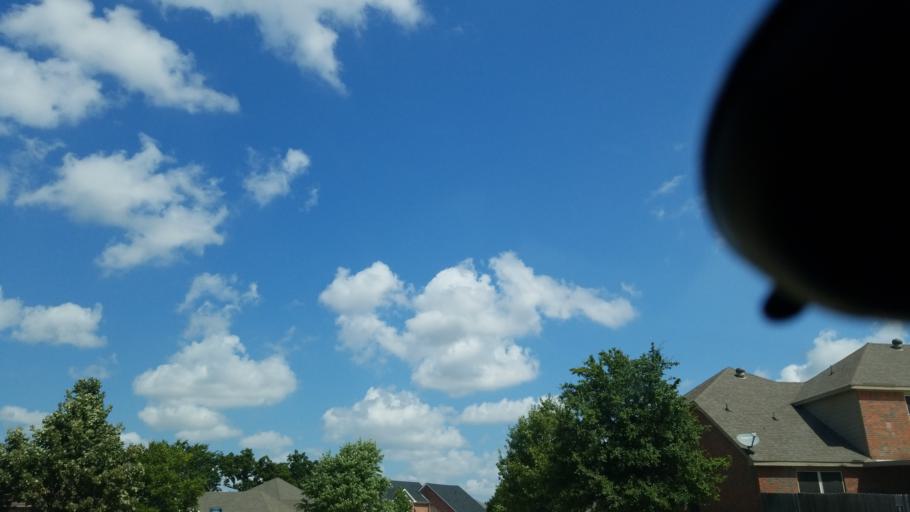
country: US
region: Texas
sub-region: Dallas County
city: Grand Prairie
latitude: 32.7229
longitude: -96.9909
